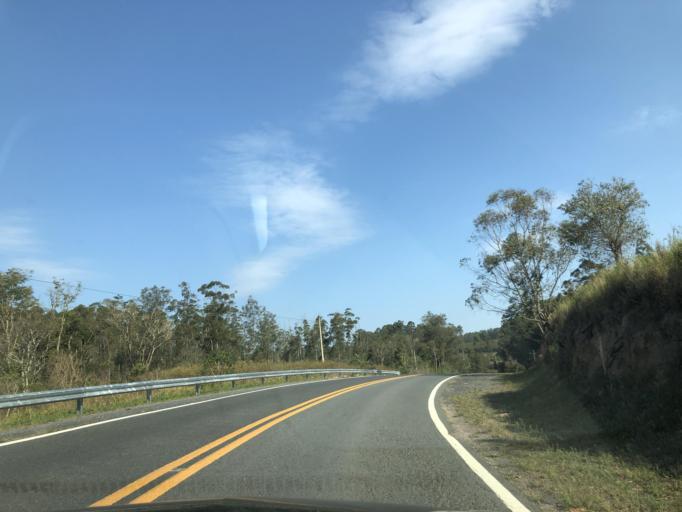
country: BR
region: Sao Paulo
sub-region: Pilar Do Sul
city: Pilar do Sul
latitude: -23.8245
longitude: -47.6638
